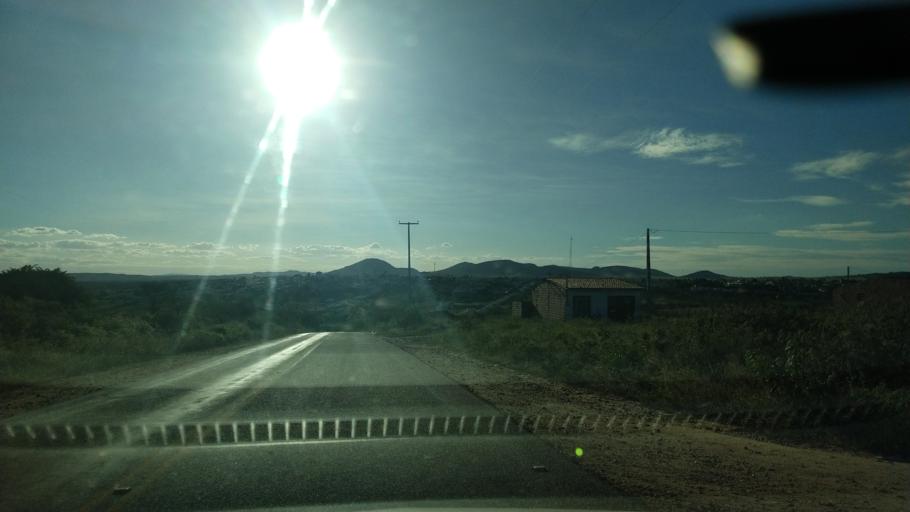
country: BR
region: Rio Grande do Norte
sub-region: Tangara
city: Tangara
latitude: -6.2090
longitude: -35.7921
